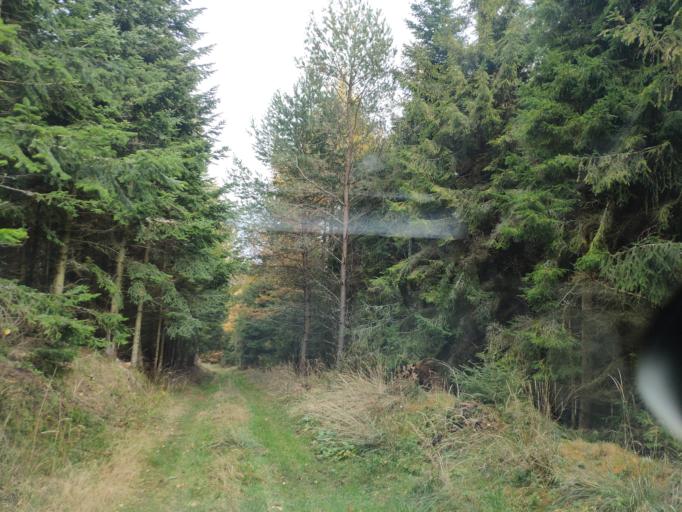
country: SK
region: Kosicky
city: Medzev
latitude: 48.7512
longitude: 20.9832
